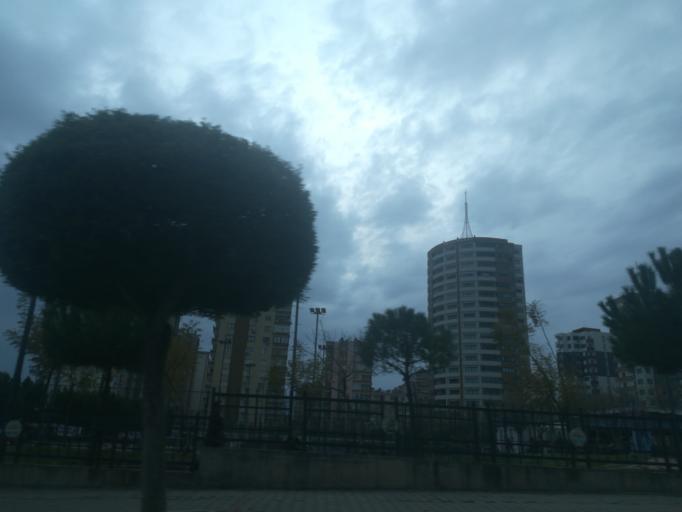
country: TR
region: Adana
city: Adana
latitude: 37.0418
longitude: 35.2918
